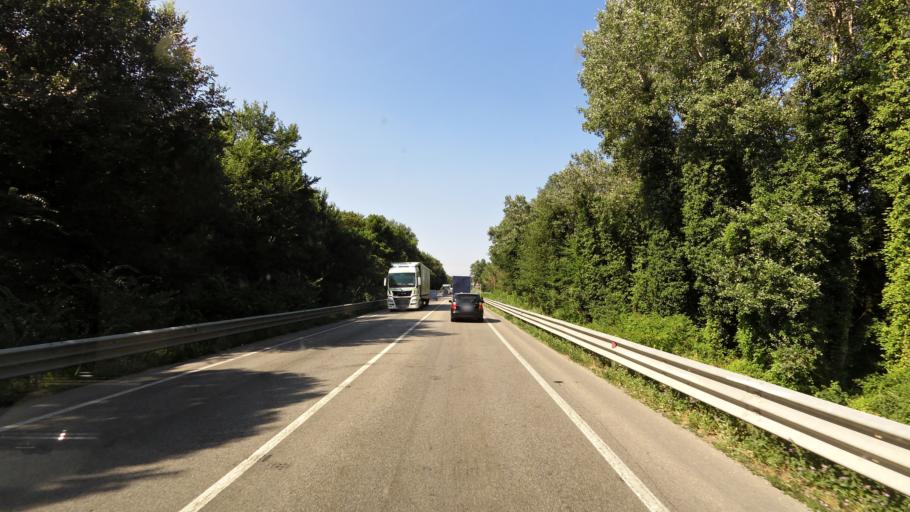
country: IT
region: Emilia-Romagna
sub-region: Provincia di Ravenna
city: Marina Romea
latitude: 44.4868
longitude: 12.2131
